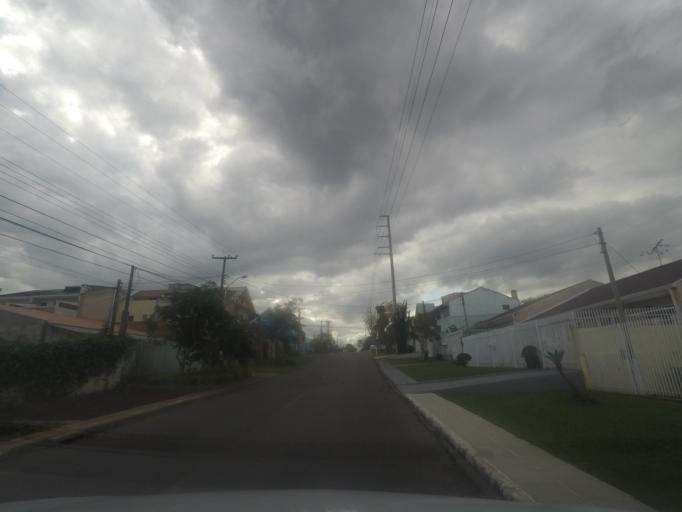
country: BR
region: Parana
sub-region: Pinhais
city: Pinhais
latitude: -25.4654
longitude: -49.2200
